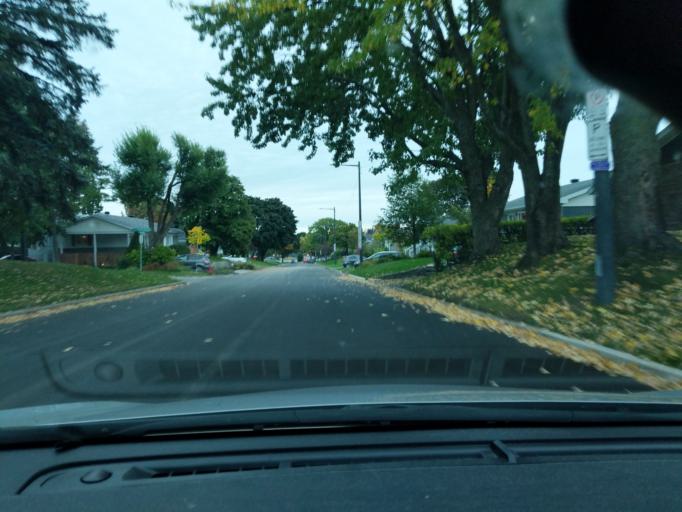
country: CA
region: Quebec
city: L'Ancienne-Lorette
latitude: 46.7654
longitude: -71.2842
